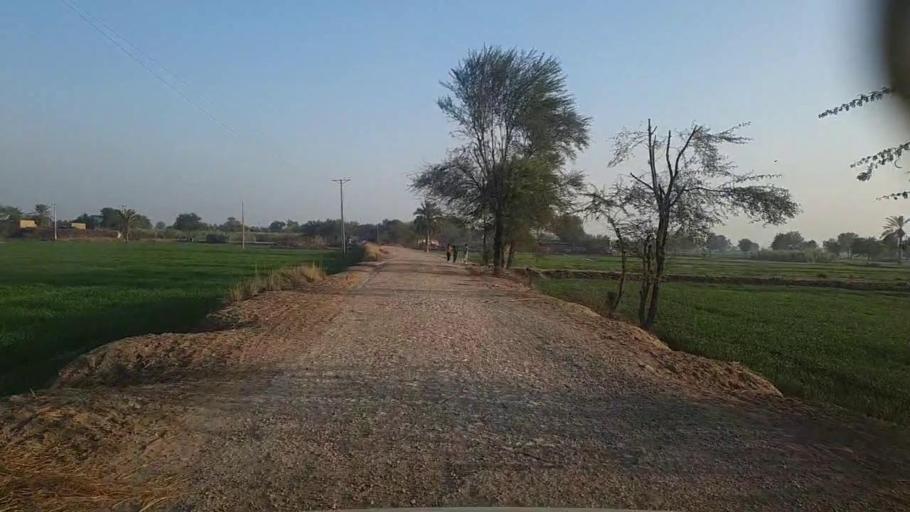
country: PK
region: Sindh
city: Khairpur
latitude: 28.0616
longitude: 69.7545
